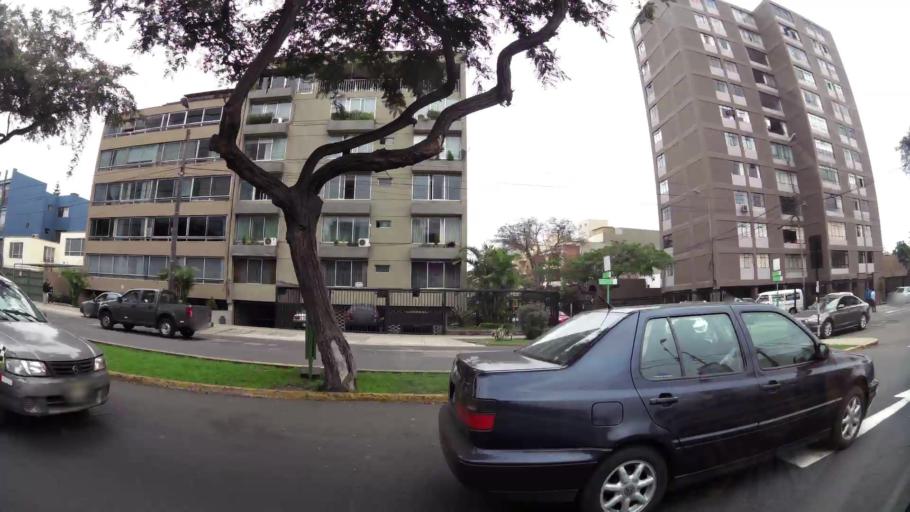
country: PE
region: Lima
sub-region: Lima
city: Surco
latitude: -12.1265
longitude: -77.0171
